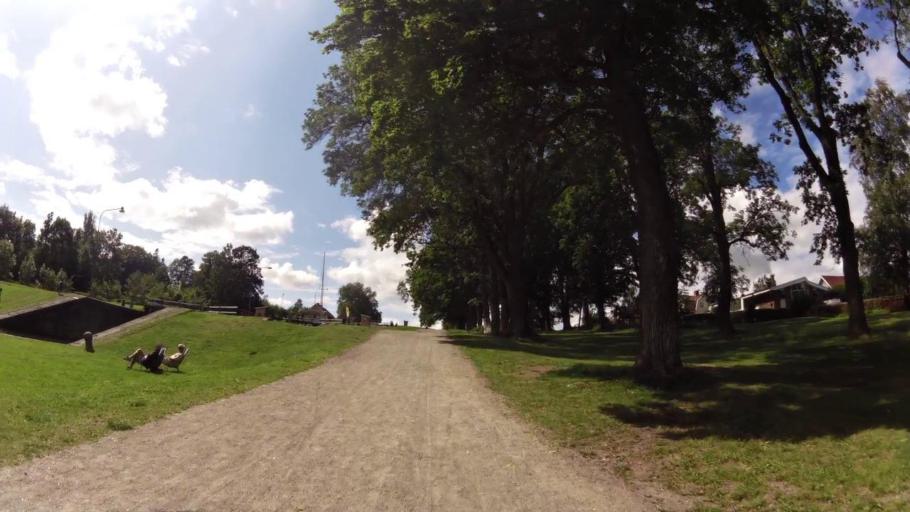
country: SE
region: OEstergoetland
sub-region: Linkopings Kommun
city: Berg
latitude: 58.4864
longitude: 15.5394
